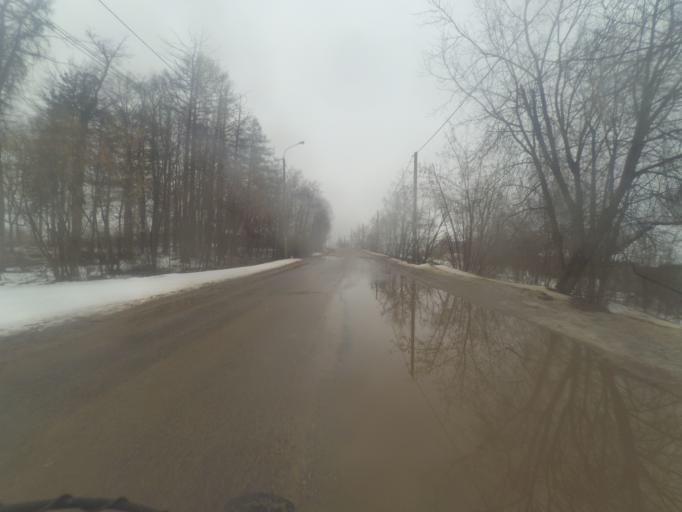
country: RU
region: Moskovskaya
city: Avtopoligon
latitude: 56.2602
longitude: 37.2526
